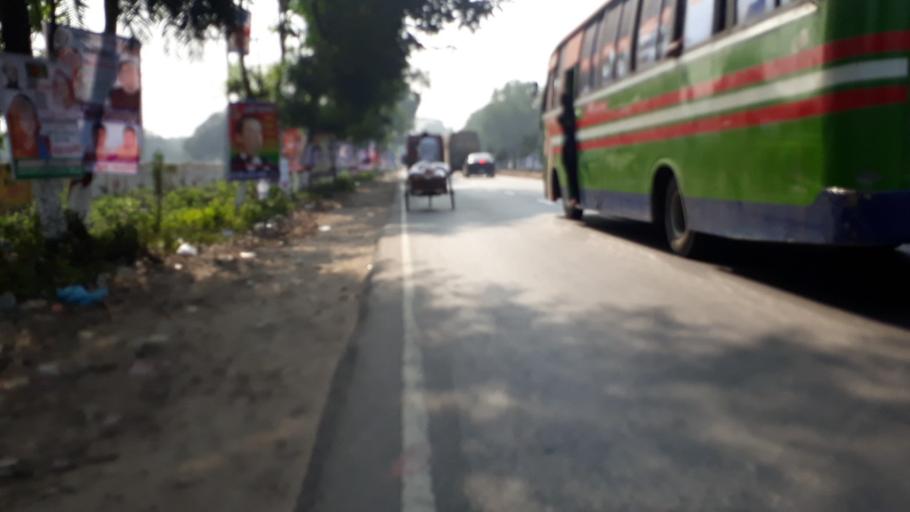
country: BD
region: Dhaka
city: Tungi
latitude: 23.8767
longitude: 90.2734
